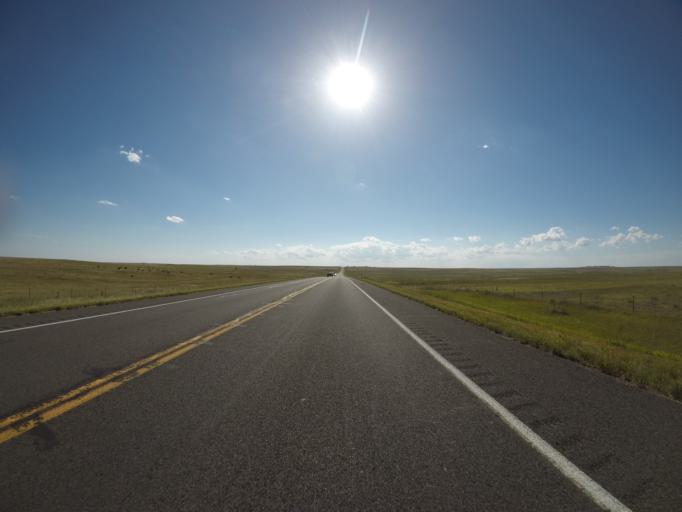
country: US
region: Colorado
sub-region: Morgan County
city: Brush
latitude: 40.6110
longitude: -103.5706
